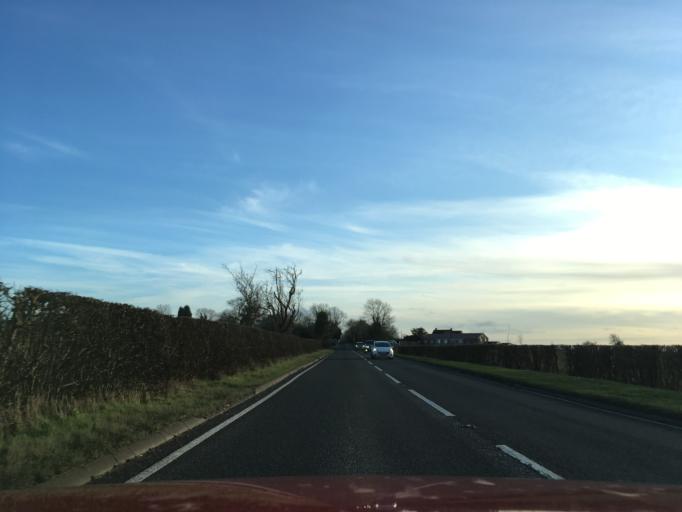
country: GB
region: England
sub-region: Warwickshire
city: Stratford-upon-Avon
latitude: 52.2343
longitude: -1.7420
